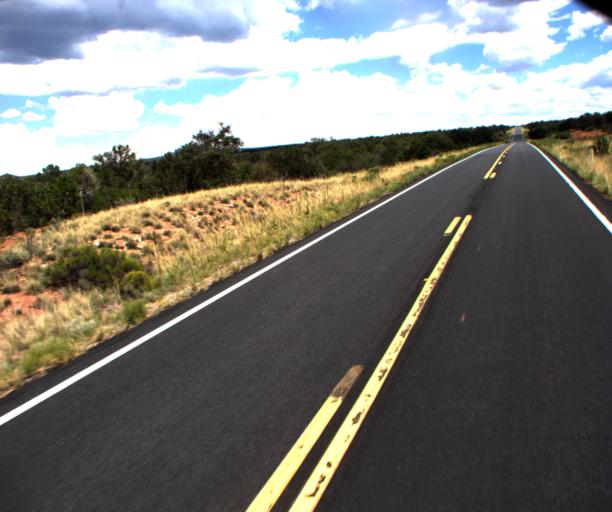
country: US
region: Arizona
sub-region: Coconino County
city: Parks
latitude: 35.6027
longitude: -112.0340
